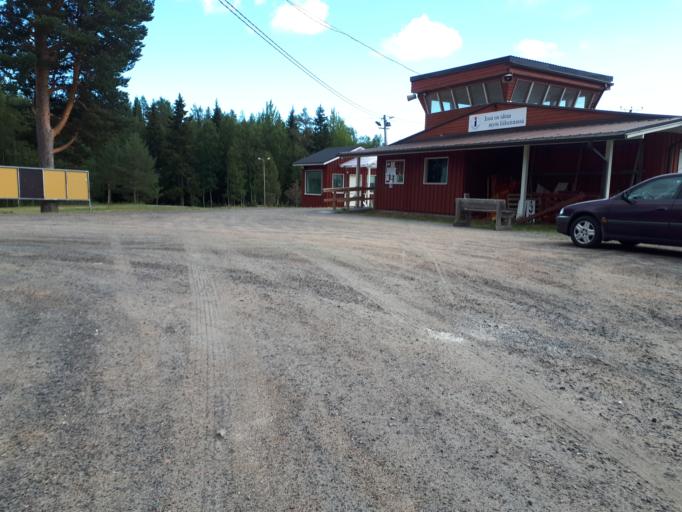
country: FI
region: Northern Ostrobothnia
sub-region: Oulunkaari
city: Ii
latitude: 65.3311
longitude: 25.3895
